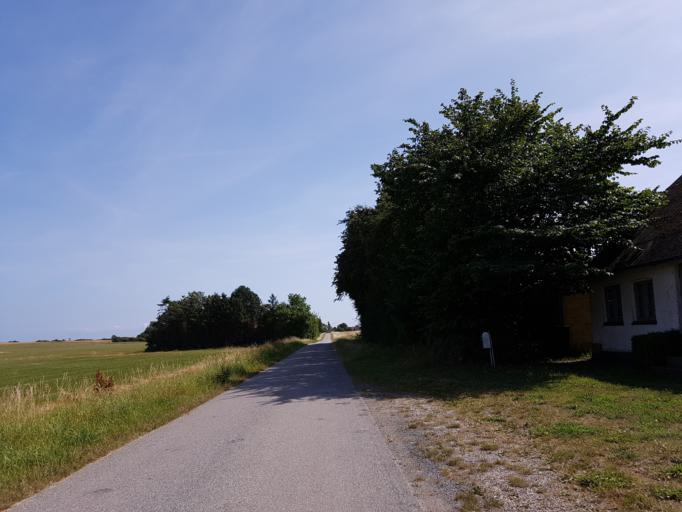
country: DK
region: Zealand
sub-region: Guldborgsund Kommune
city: Nykobing Falster
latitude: 54.5756
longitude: 11.9622
